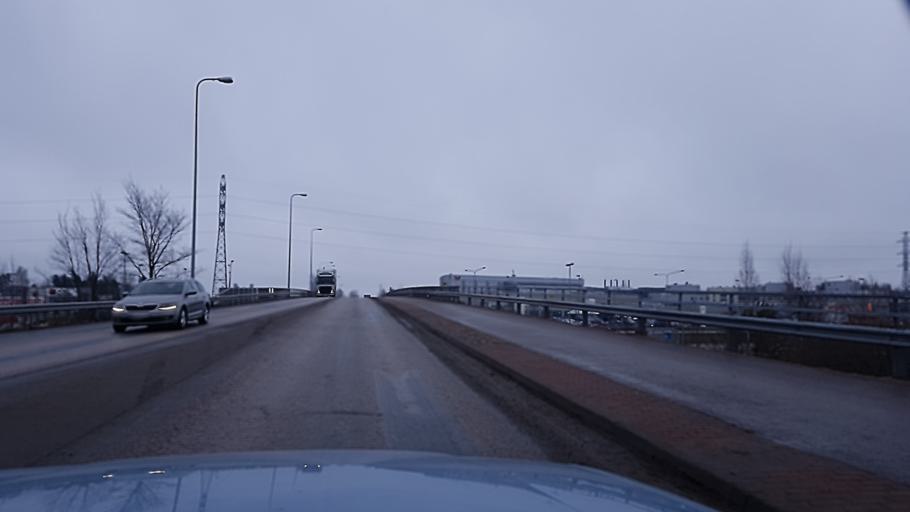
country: FI
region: Uusimaa
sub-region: Helsinki
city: Vantaa
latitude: 60.2953
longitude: 24.9820
